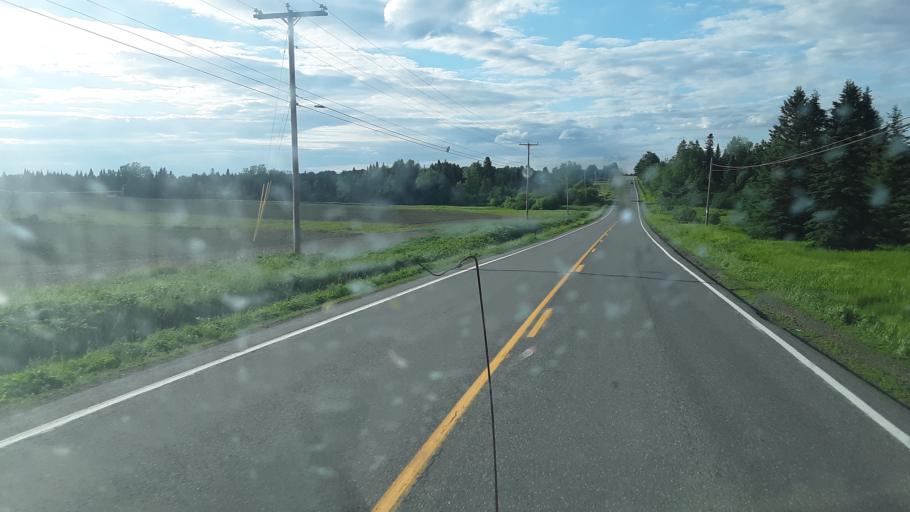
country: US
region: Maine
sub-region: Aroostook County
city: Presque Isle
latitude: 46.6101
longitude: -68.3977
